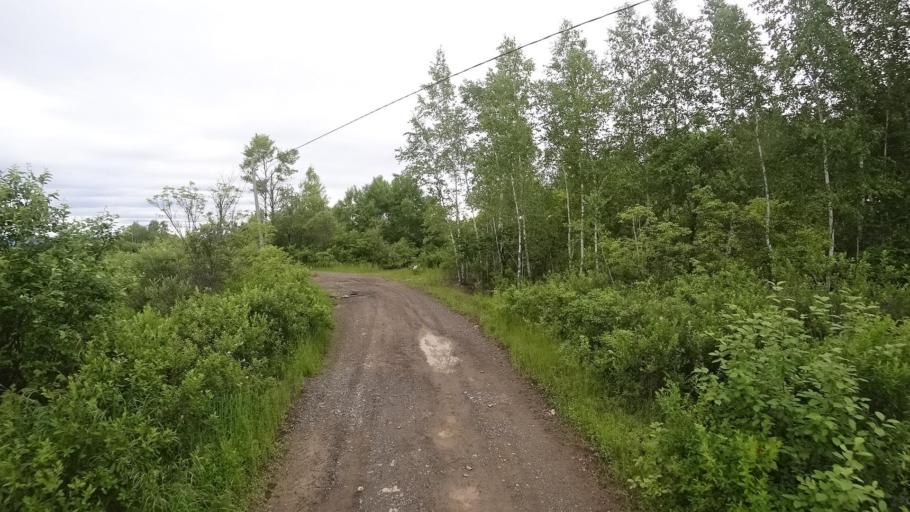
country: RU
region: Khabarovsk Krai
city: Amursk
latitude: 49.8951
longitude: 136.1462
